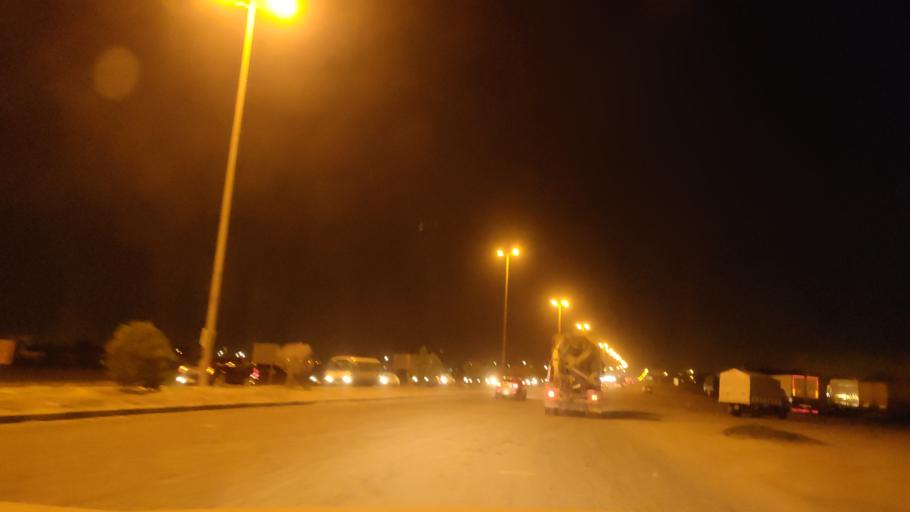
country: KW
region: Al Asimah
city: Ar Rabiyah
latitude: 29.2497
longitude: 47.8454
